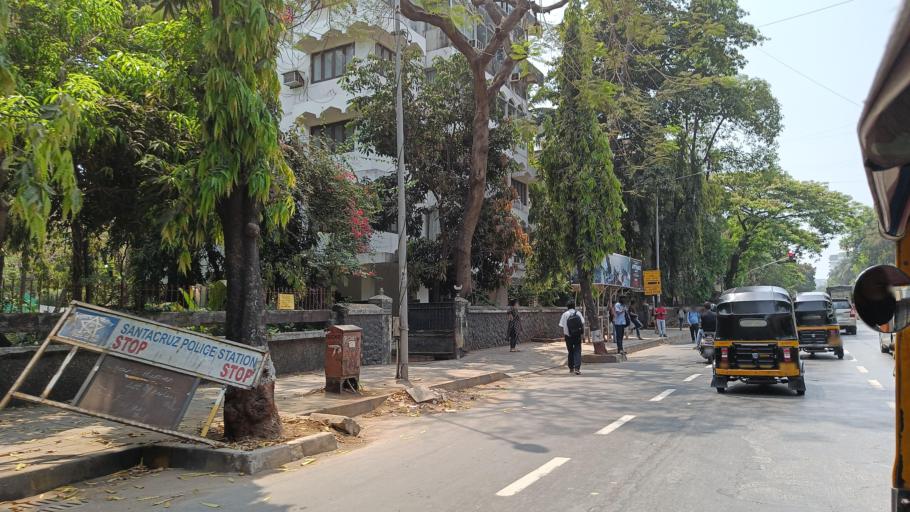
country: IN
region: Maharashtra
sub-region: Mumbai Suburban
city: Mumbai
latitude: 19.0794
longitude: 72.8344
